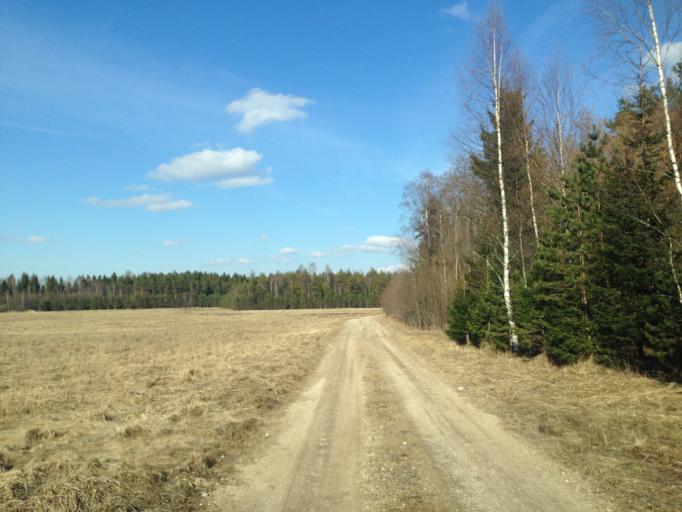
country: EE
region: Harju
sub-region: Keila linn
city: Keila
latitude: 59.1744
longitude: 24.4528
